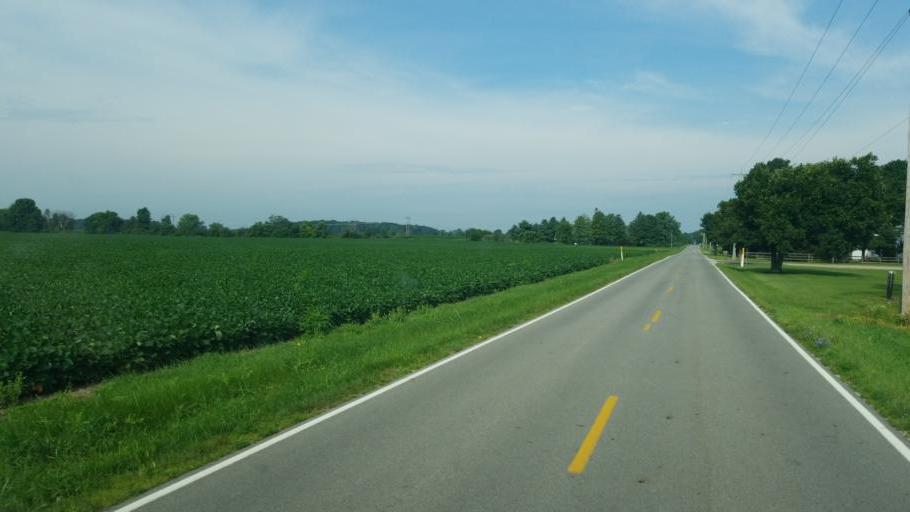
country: US
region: Ohio
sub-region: Marion County
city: Prospect
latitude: 40.5204
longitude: -83.1747
